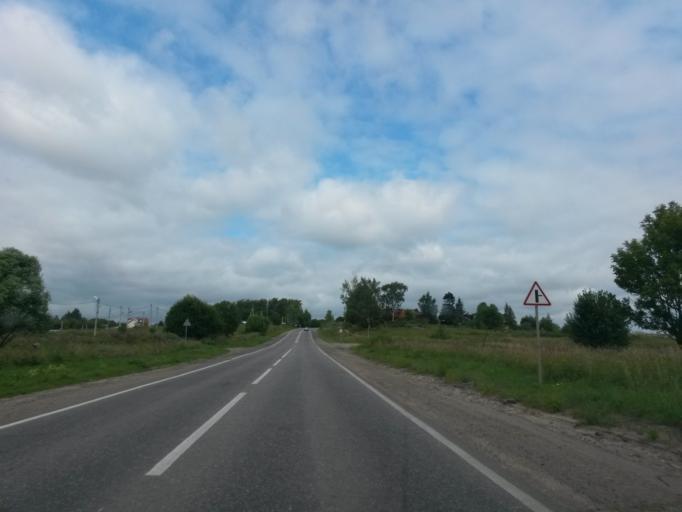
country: RU
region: Jaroslavl
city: Yaroslavl
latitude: 57.5403
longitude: 39.8659
